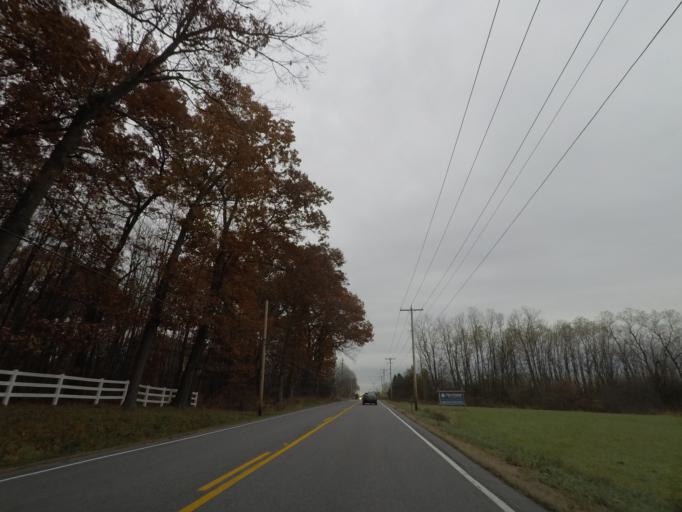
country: US
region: New York
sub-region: Schenectady County
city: East Glenville
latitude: 42.8938
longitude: -73.8679
